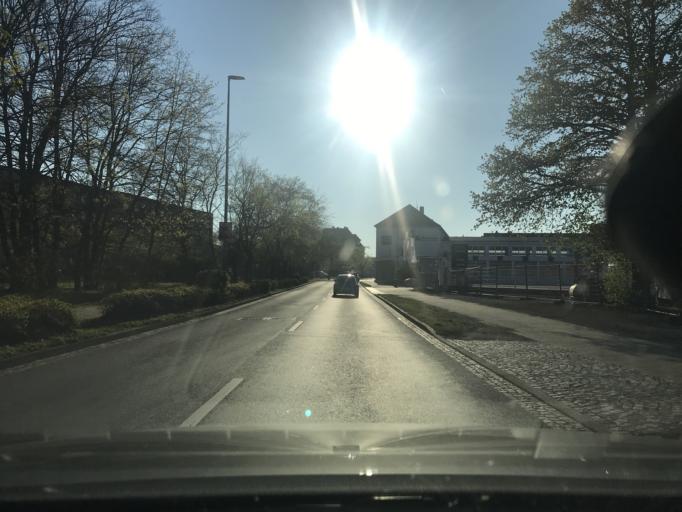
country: DE
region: Thuringia
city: Nordhausen
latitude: 51.4956
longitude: 10.8007
